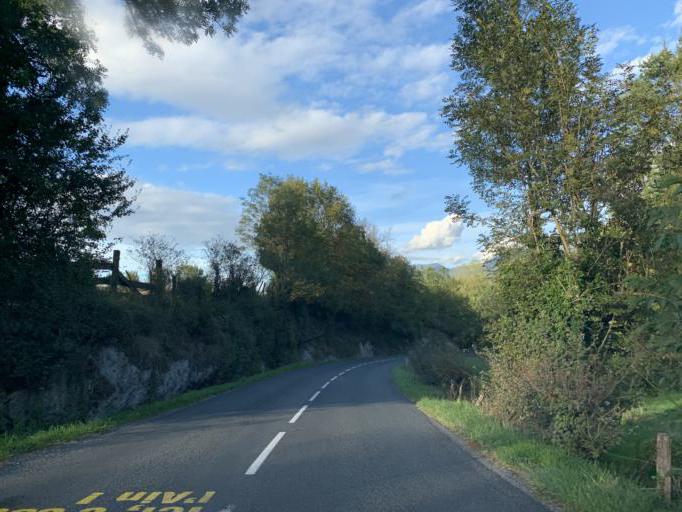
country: FR
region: Rhone-Alpes
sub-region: Departement de l'Ain
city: Artemare
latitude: 45.8527
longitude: 5.6795
